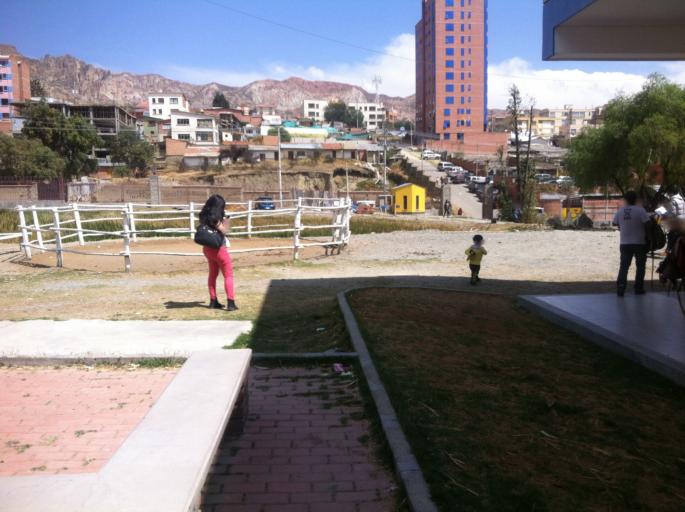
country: BO
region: La Paz
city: La Paz
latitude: -16.5388
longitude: -68.0659
